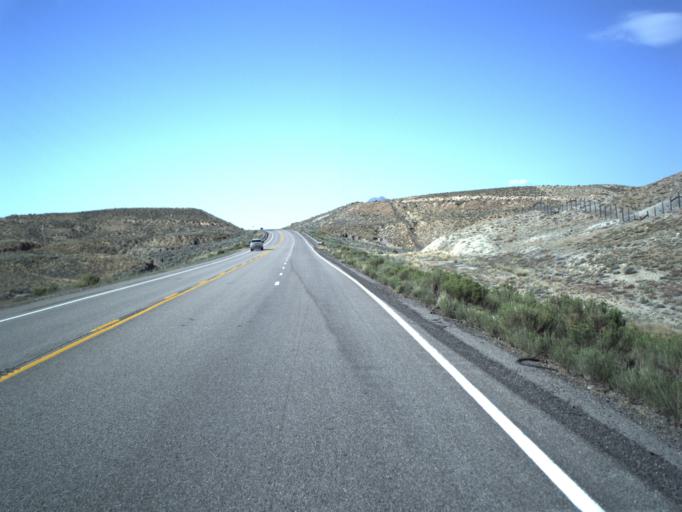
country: US
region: Utah
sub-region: Emery County
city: Huntington
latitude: 39.4098
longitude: -110.8812
